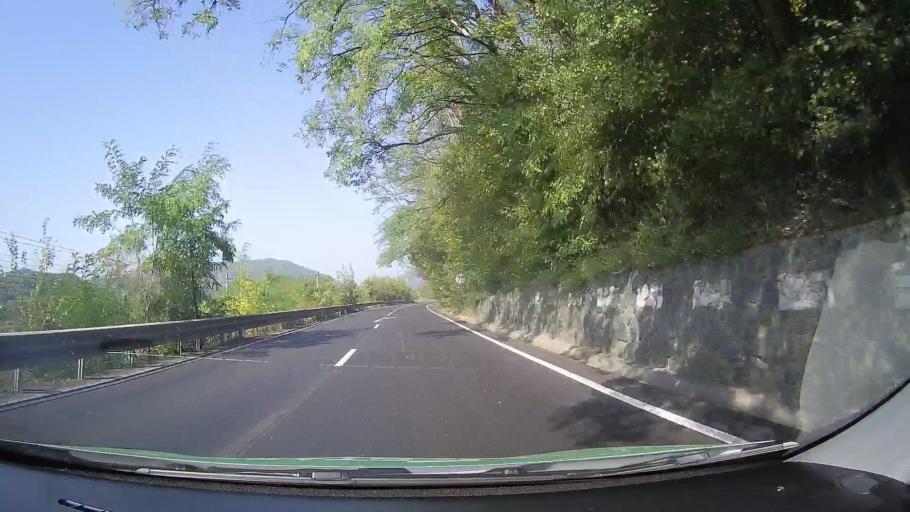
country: RO
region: Hunedoara
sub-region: Comuna Burjuc
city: Burjuc
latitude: 45.9448
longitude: 22.4962
